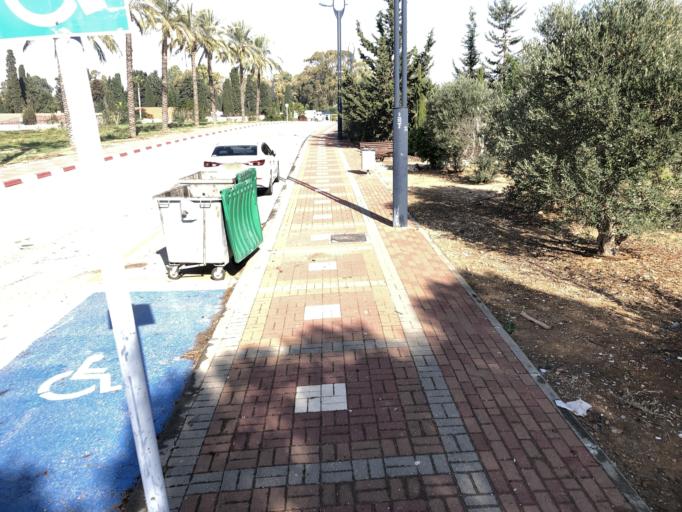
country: IL
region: Northern District
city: `Akko
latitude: 32.9388
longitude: 35.0923
